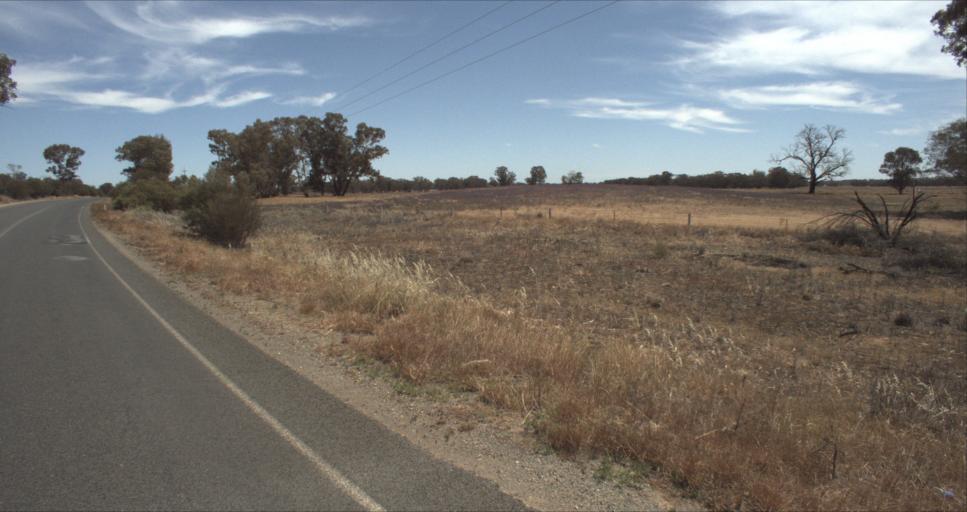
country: AU
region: New South Wales
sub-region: Leeton
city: Leeton
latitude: -34.6590
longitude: 146.4562
